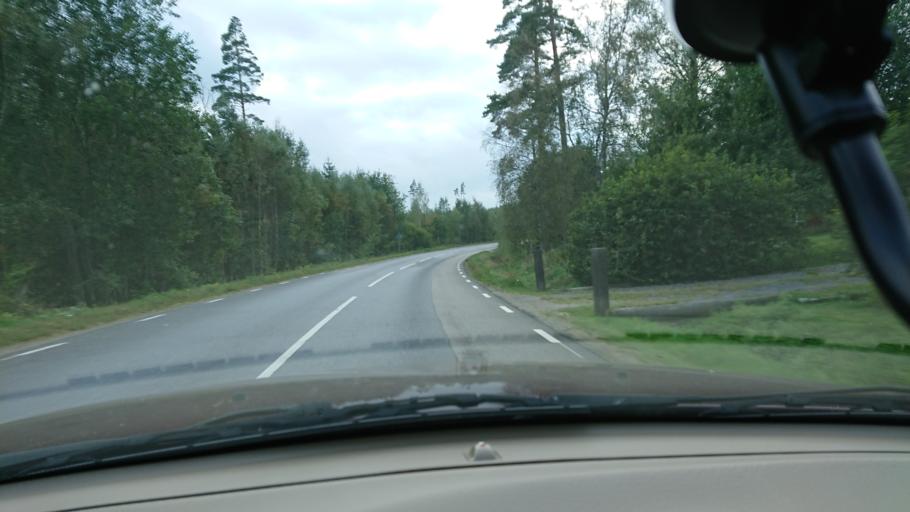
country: SE
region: Kronoberg
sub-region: Vaxjo Kommun
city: Lammhult
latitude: 57.0836
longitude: 14.7051
